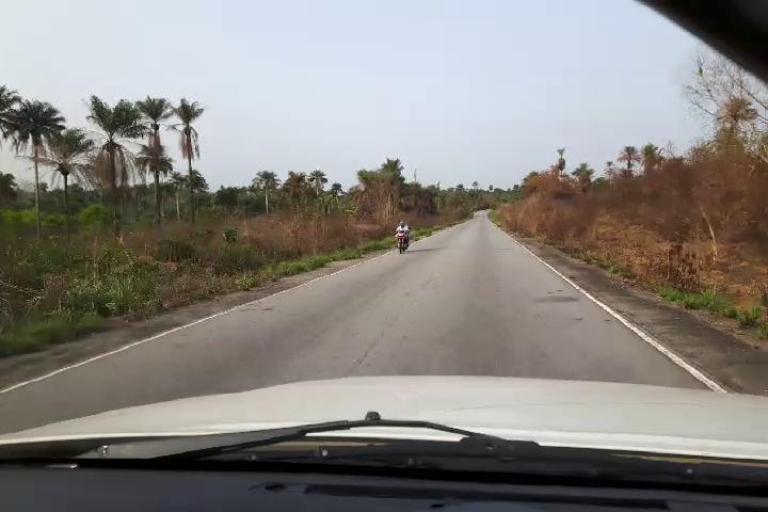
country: SL
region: Eastern Province
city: Blama
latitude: 7.9401
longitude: -11.5068
